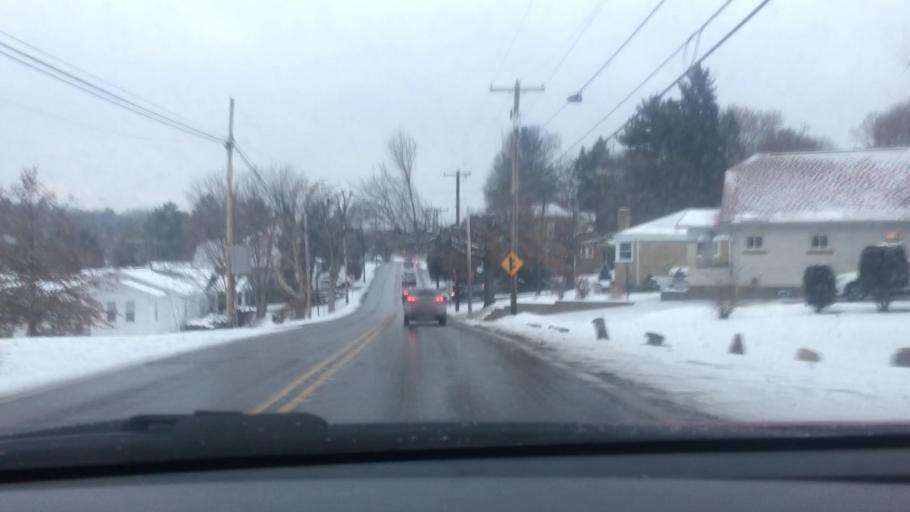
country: US
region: Pennsylvania
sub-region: Allegheny County
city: Bethel Park
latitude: 40.3426
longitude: -80.0236
